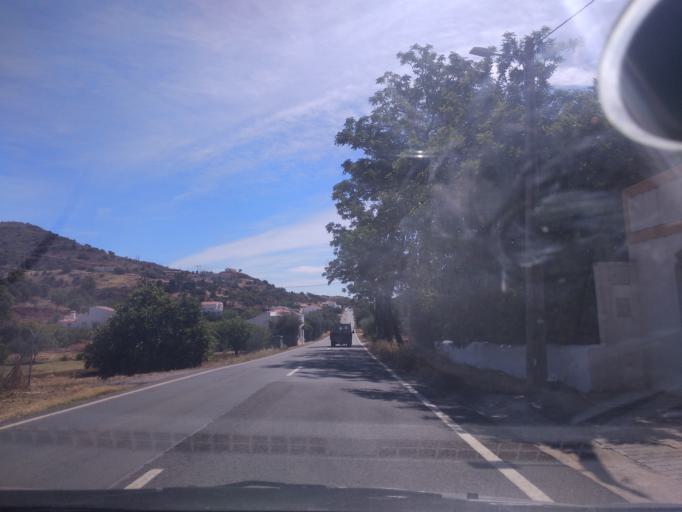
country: PT
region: Faro
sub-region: Olhao
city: Moncarapacho
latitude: 37.1528
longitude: -7.7995
